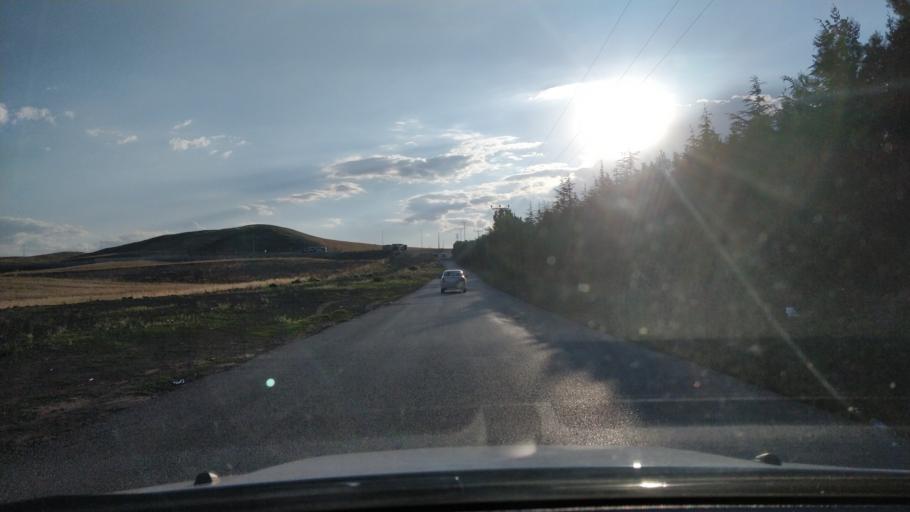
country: TR
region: Ankara
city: Etimesgut
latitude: 39.8270
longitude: 32.5600
